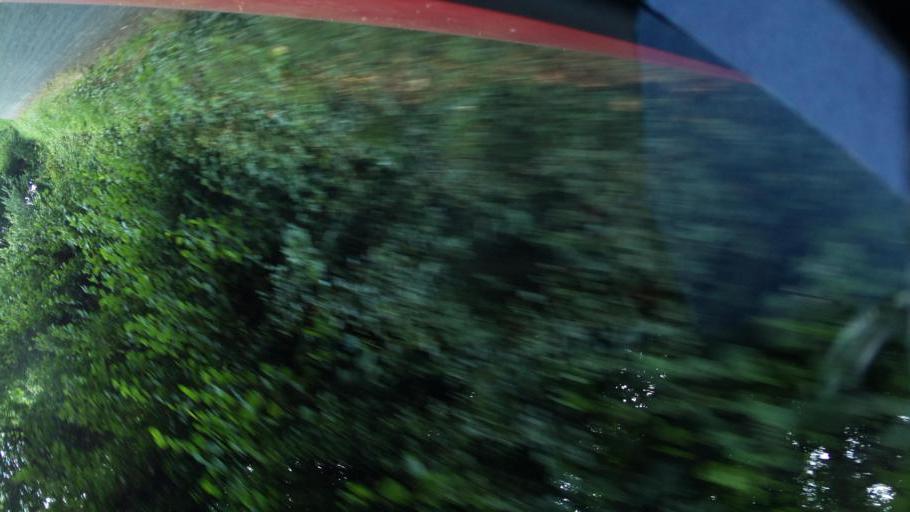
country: GB
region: England
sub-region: Somerset
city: Evercreech
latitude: 51.1702
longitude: -2.5061
